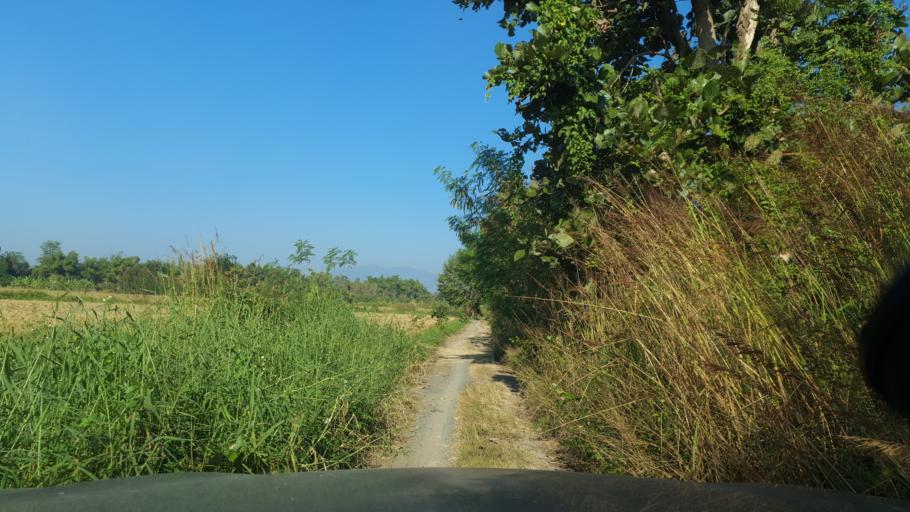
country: TH
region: Chiang Mai
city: Saraphi
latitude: 18.7121
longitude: 99.0778
